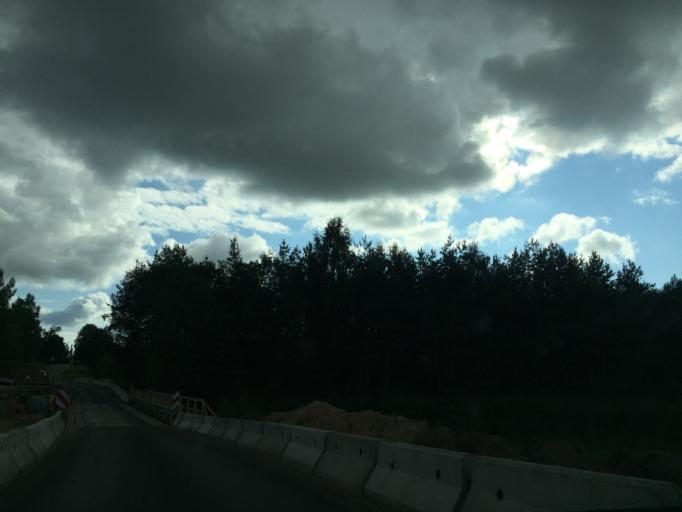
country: LV
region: Limbazu Rajons
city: Limbazi
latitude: 57.3536
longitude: 24.6667
